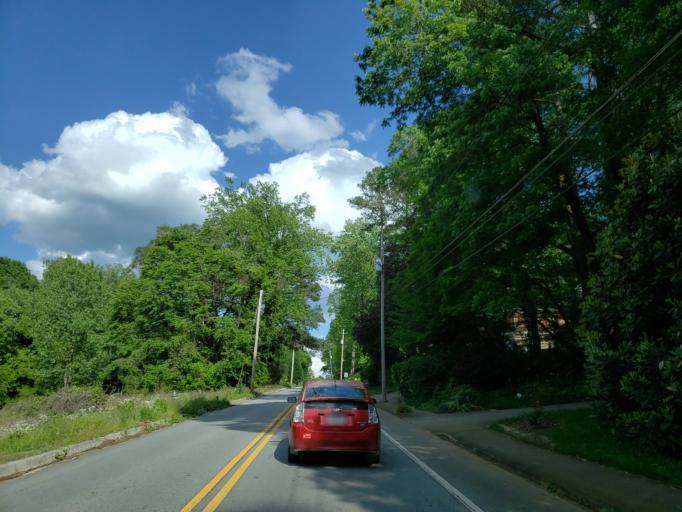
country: US
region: Georgia
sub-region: DeKalb County
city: North Druid Hills
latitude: 33.8469
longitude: -84.2779
